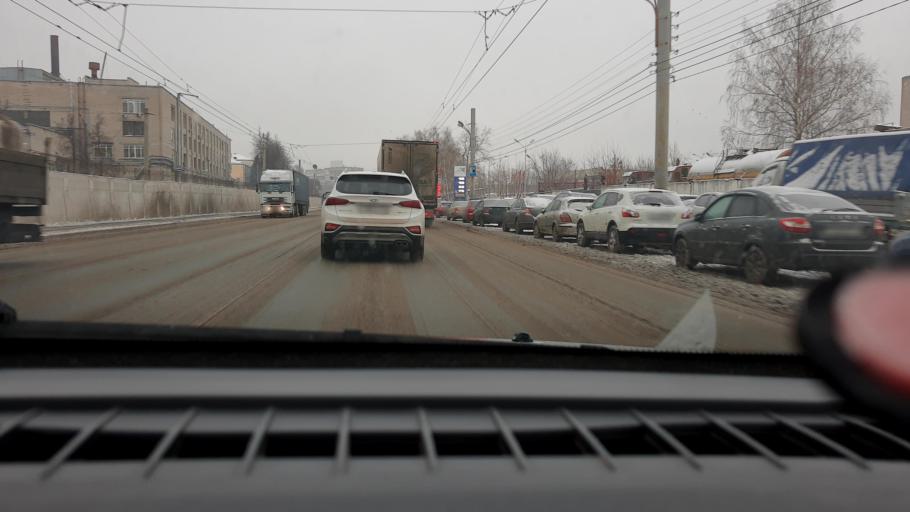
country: RU
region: Nizjnij Novgorod
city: Nizhniy Novgorod
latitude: 56.3212
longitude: 43.9091
